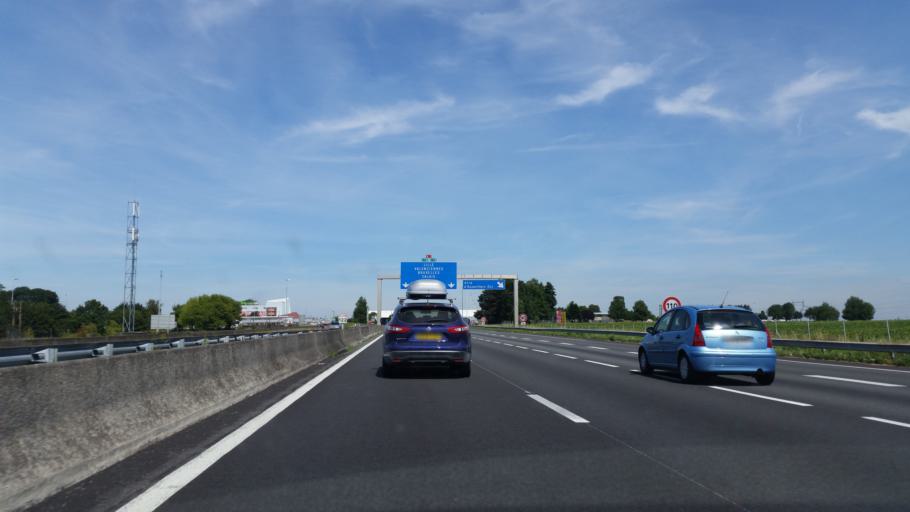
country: FR
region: Picardie
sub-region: Departement de la Somme
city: Chaulnes
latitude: 49.8830
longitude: 2.8377
